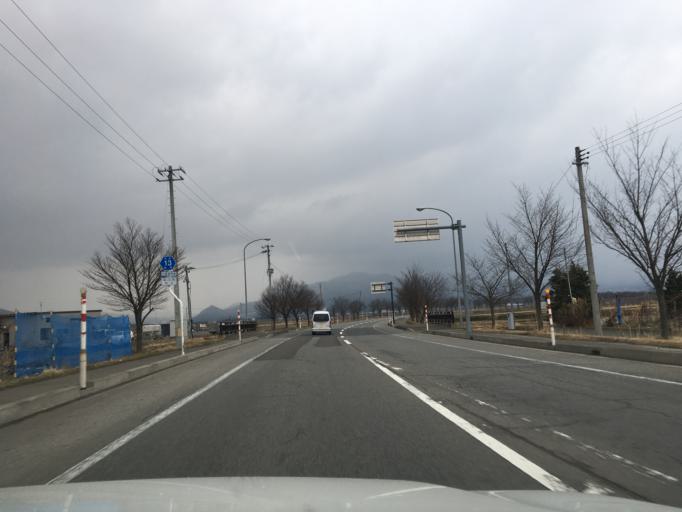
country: JP
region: Aomori
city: Kuroishi
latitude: 40.5712
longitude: 140.5675
